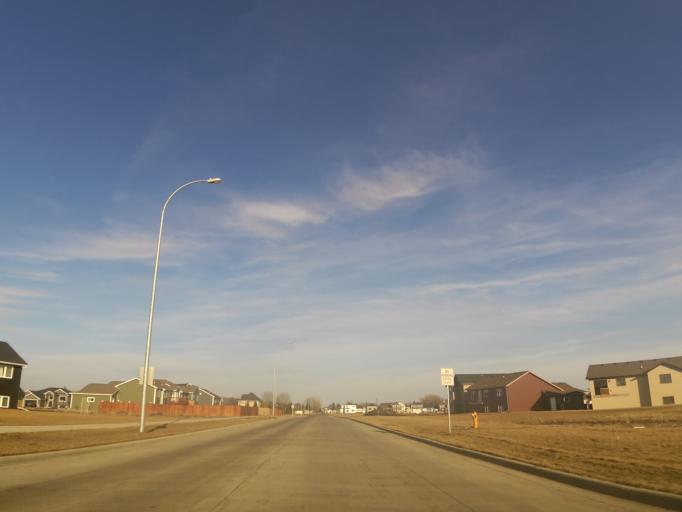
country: US
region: North Dakota
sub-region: Grand Forks County
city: Grand Forks
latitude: 47.8676
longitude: -97.0408
